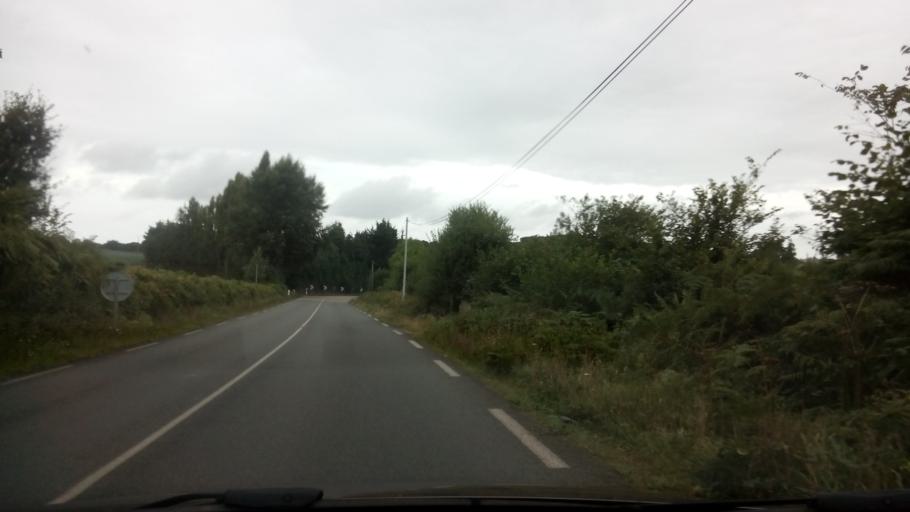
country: FR
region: Brittany
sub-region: Departement du Finistere
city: Morlaix
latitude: 48.6085
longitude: -3.7959
